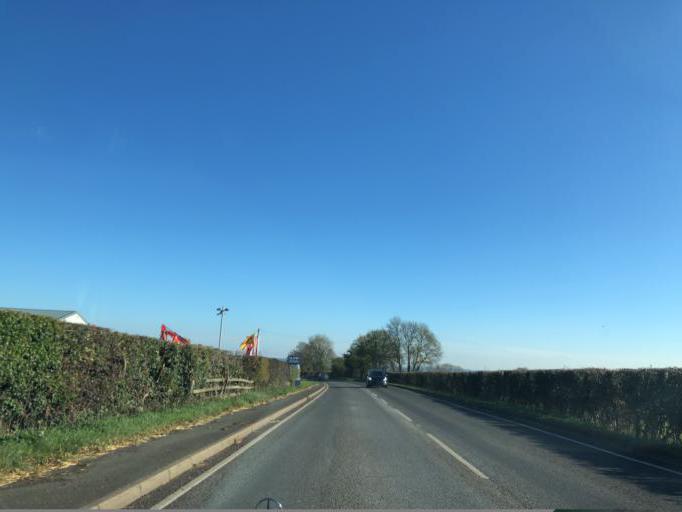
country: GB
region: England
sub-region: Warwickshire
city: Harbury
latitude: 52.2558
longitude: -1.4405
